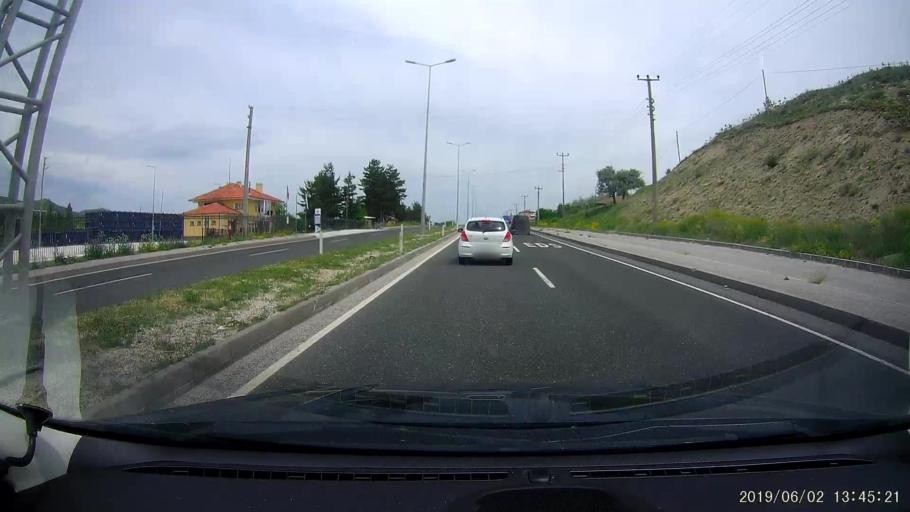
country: TR
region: Cankiri
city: Kursunlu
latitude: 40.8456
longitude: 33.2490
